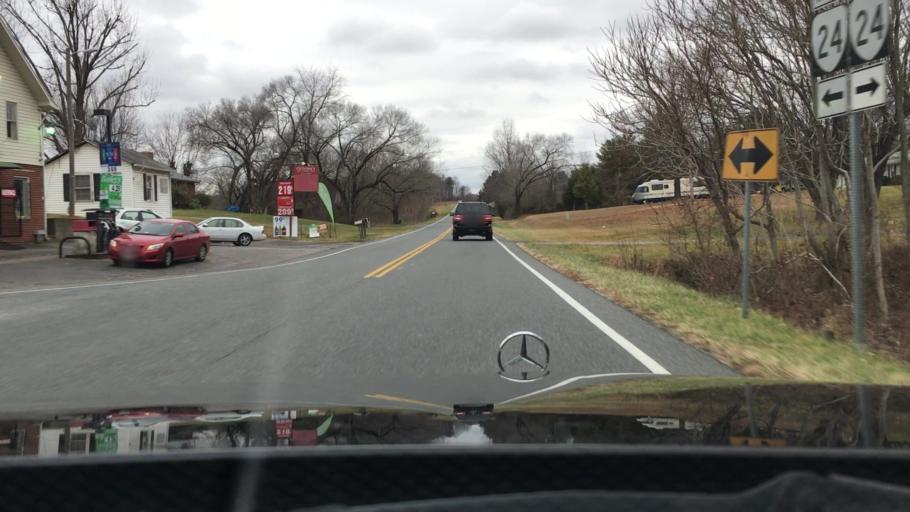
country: US
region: Virginia
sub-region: Franklin County
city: North Shore
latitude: 37.2428
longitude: -79.6741
